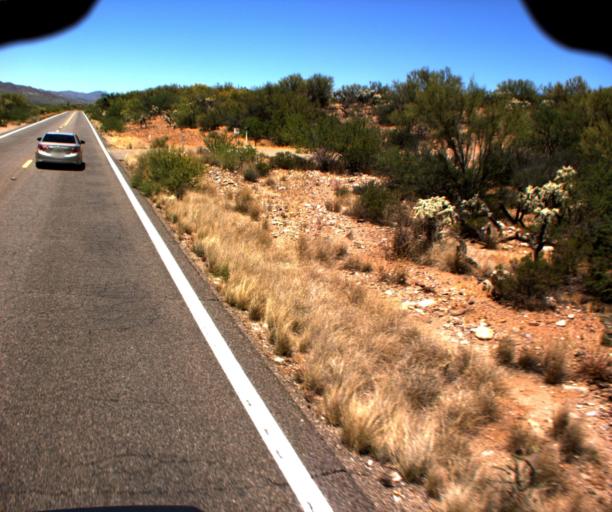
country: US
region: Arizona
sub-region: Pinal County
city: Kearny
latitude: 33.1099
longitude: -110.7638
